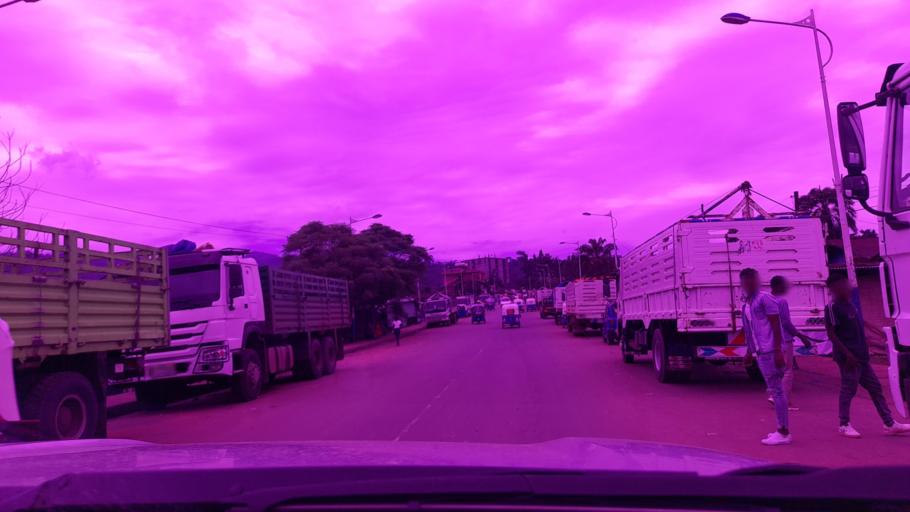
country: ET
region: Southern Nations, Nationalities, and People's Region
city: Mizan Teferi
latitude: 6.9960
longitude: 35.5943
